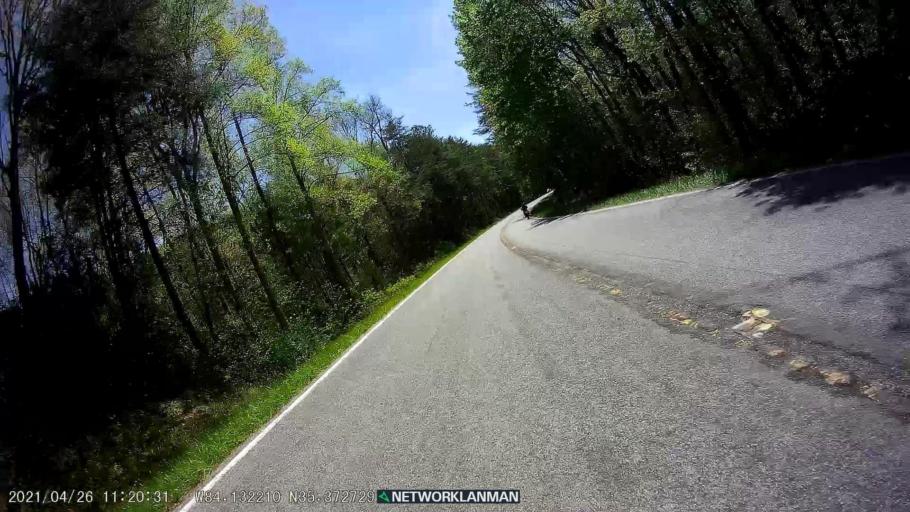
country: US
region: Tennessee
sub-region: Monroe County
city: Vonore
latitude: 35.3729
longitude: -84.1321
